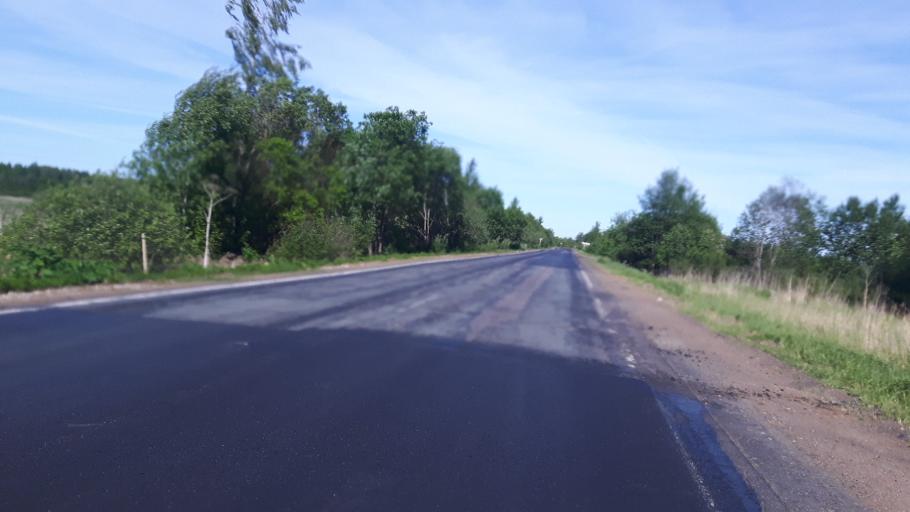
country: RU
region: Leningrad
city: Ivangorod
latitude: 59.4166
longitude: 28.3351
